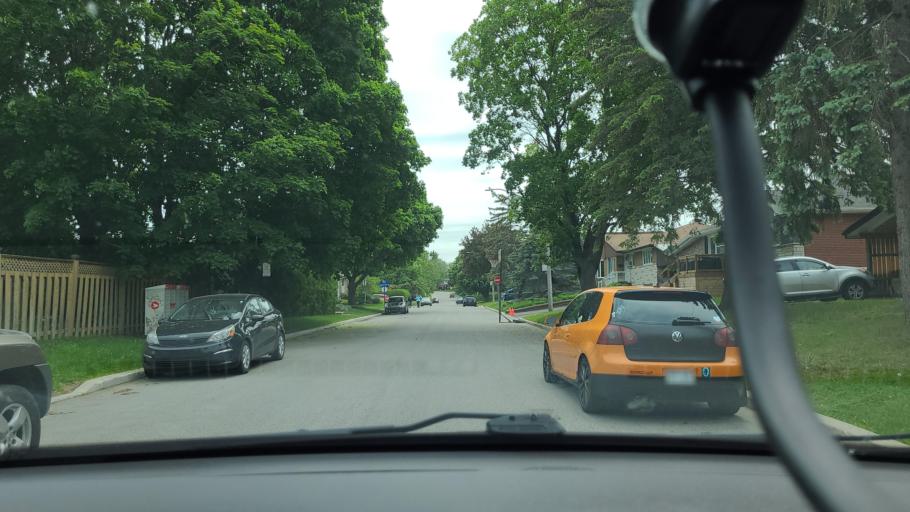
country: CA
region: Quebec
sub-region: Laurentides
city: Rosemere
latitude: 45.6059
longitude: -73.8040
